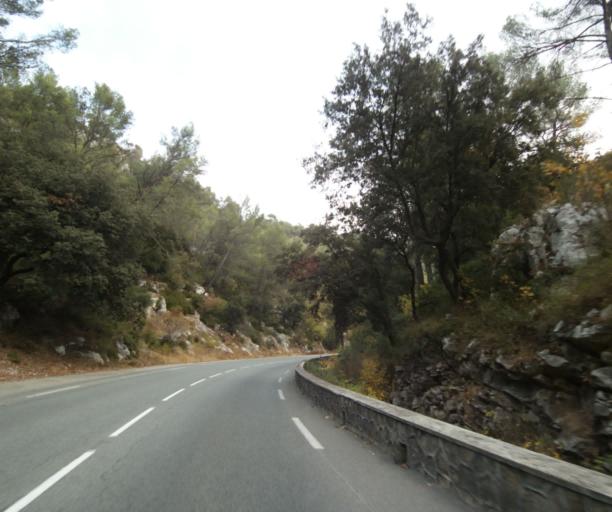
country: FR
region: Provence-Alpes-Cote d'Azur
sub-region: Departement des Bouches-du-Rhone
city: Cuges-les-Pins
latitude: 43.2675
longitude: 5.6601
